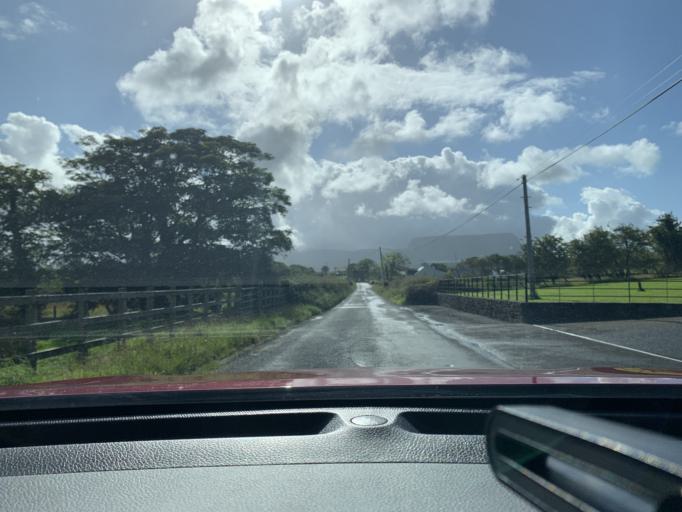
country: IE
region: Connaught
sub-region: Sligo
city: Strandhill
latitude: 54.3921
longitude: -8.5472
